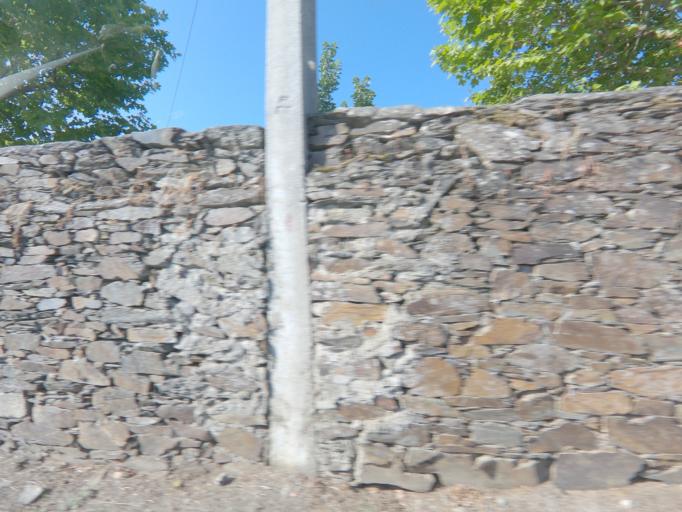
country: PT
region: Vila Real
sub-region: Sabrosa
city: Vilela
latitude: 41.2299
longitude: -7.5653
